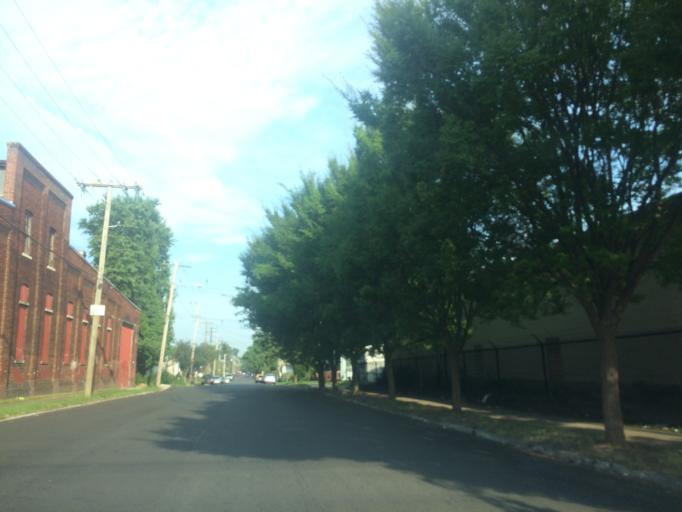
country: US
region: Kentucky
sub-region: Jefferson County
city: Louisville
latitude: 38.2302
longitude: -85.7421
